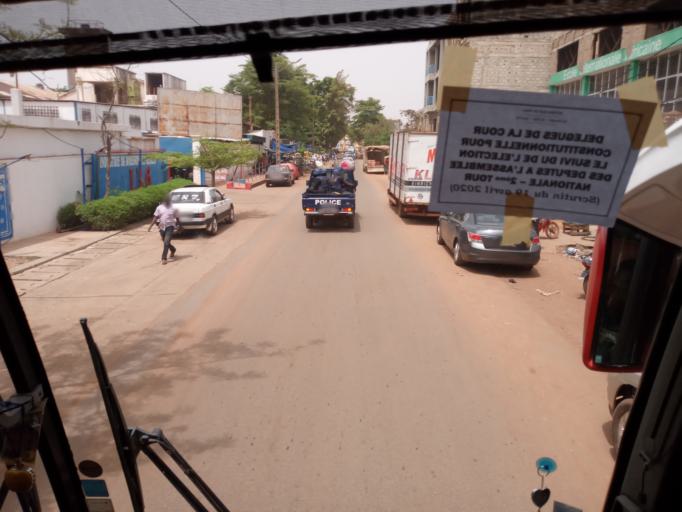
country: ML
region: Bamako
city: Bamako
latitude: 12.6374
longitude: -8.0006
